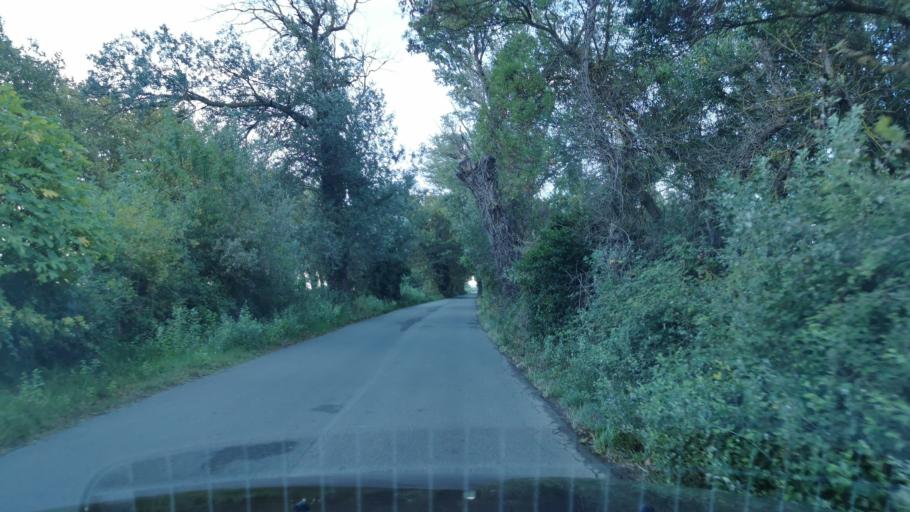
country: FR
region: Languedoc-Roussillon
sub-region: Departement de l'Aude
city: Gruissan
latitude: 43.1285
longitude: 3.0313
